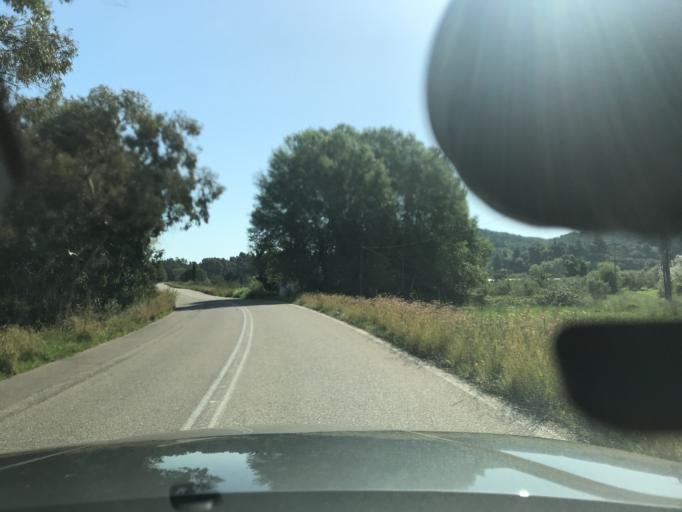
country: GR
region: West Greece
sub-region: Nomos Ileias
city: Epitalion
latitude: 37.6424
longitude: 21.5022
